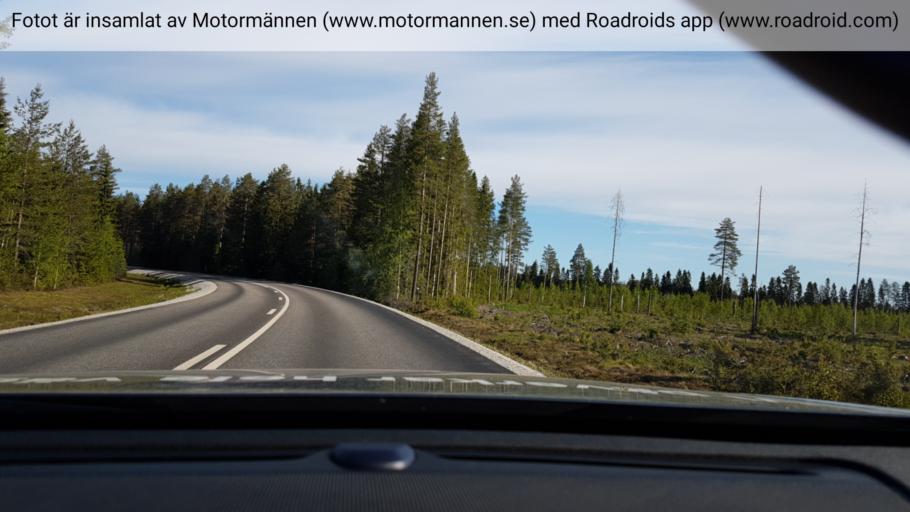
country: SE
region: Vaesterbotten
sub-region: Vindelns Kommun
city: Vindeln
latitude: 64.0799
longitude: 19.6332
